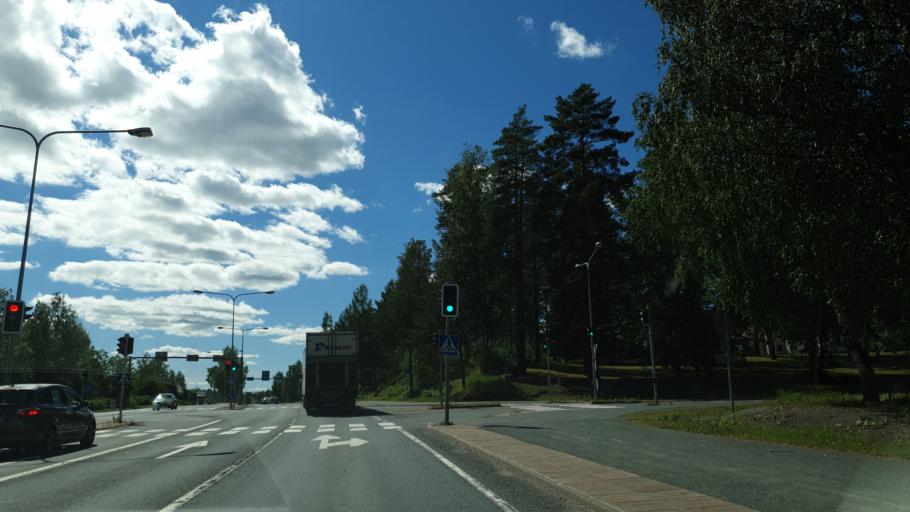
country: FI
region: Northern Savo
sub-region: Kuopio
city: Siilinjaervi
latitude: 63.0764
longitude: 27.6591
